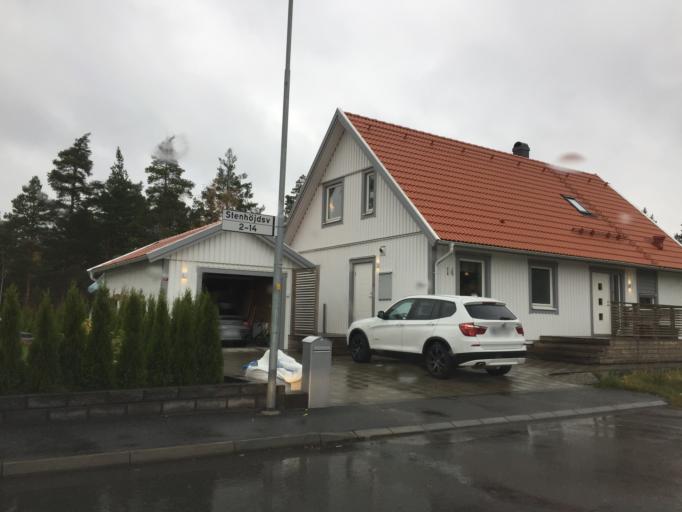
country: SE
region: Vaestra Goetaland
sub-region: Trollhattan
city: Trollhattan
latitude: 58.3223
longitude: 12.2915
